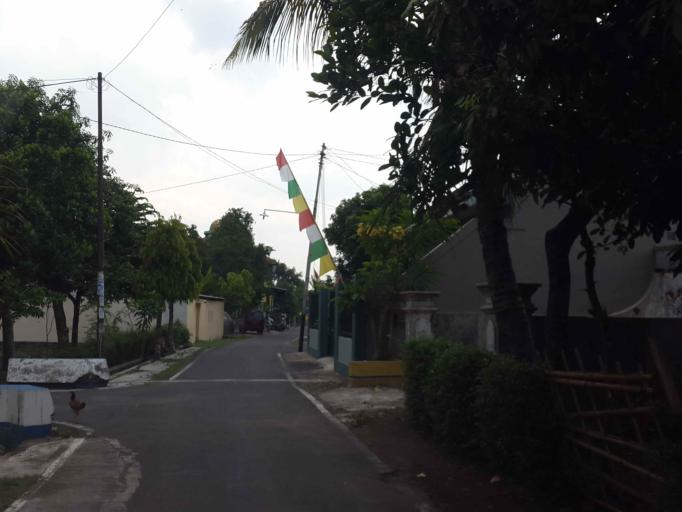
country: ID
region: Central Java
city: Jaten
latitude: -7.5912
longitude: 110.9372
